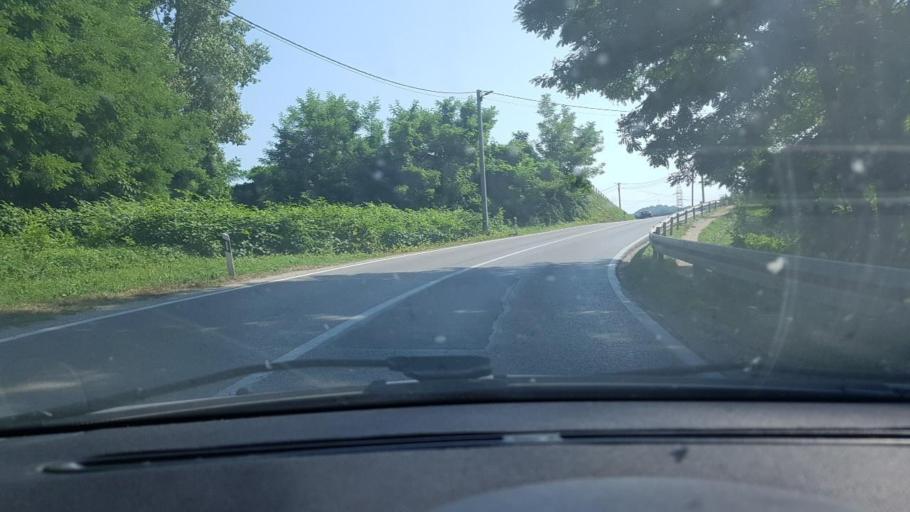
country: BA
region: Federation of Bosnia and Herzegovina
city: Velika Kladusa
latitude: 45.1728
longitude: 15.8175
